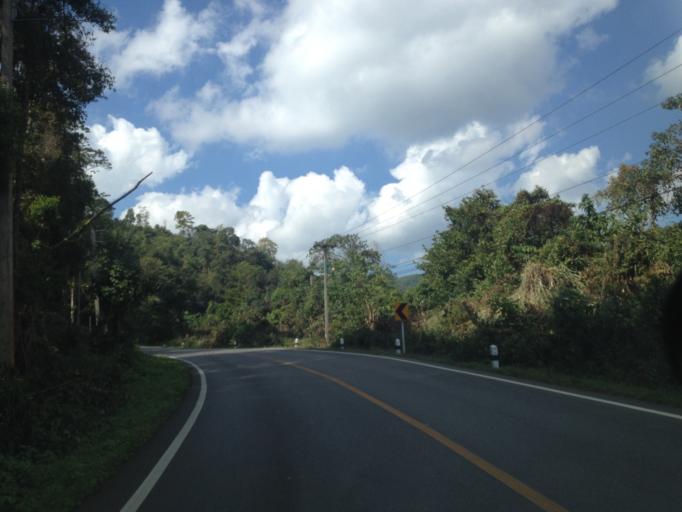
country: TH
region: Mae Hong Son
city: Ban Huai I Huak
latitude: 18.1480
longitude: 98.1472
